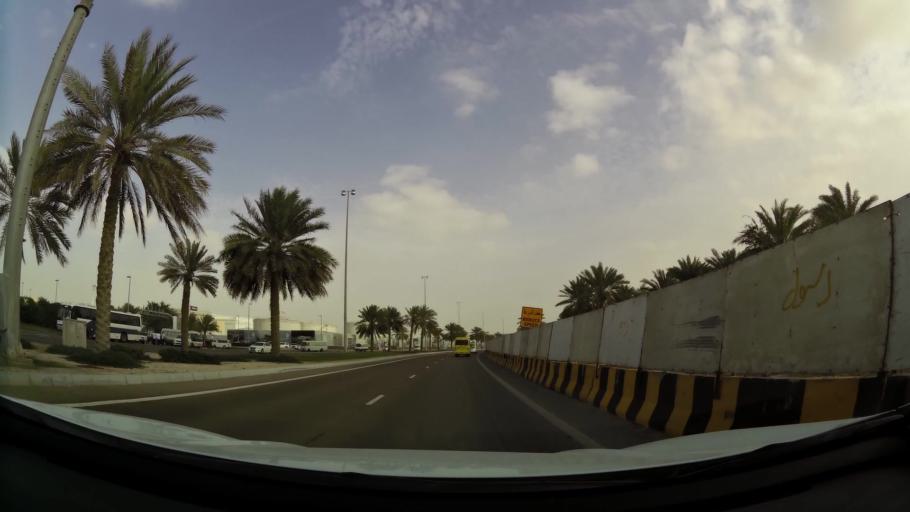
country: AE
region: Abu Dhabi
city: Abu Dhabi
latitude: 24.4330
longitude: 54.6322
